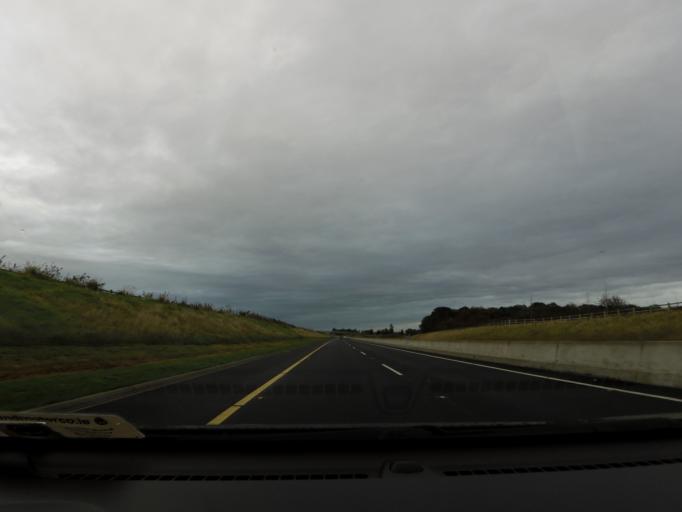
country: IE
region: Connaught
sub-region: County Galway
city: Athenry
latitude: 53.3332
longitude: -8.8029
